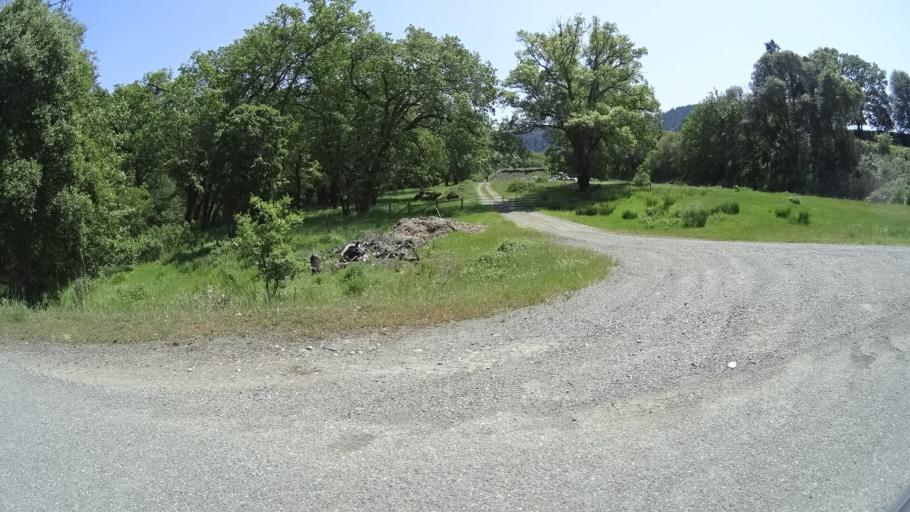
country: US
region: California
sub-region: Humboldt County
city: Redway
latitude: 40.2165
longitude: -123.6343
